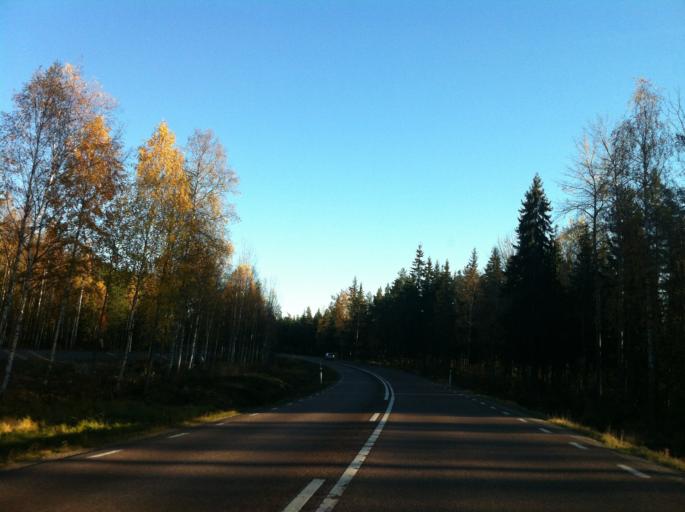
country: SE
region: Dalarna
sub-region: Faluns Kommun
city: Grycksbo
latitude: 60.6740
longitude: 15.5121
